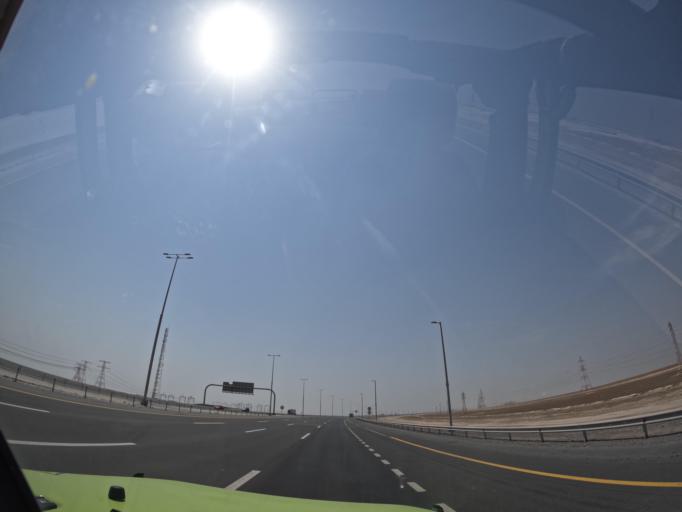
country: AE
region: Abu Dhabi
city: Abu Dhabi
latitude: 24.1588
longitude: 54.3491
